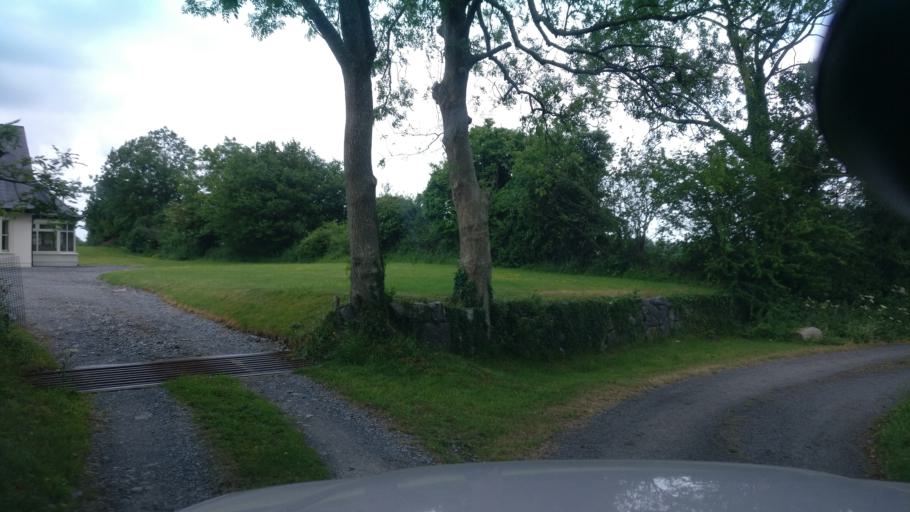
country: IE
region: Connaught
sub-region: County Galway
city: Ballinasloe
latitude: 53.2976
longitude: -8.2861
